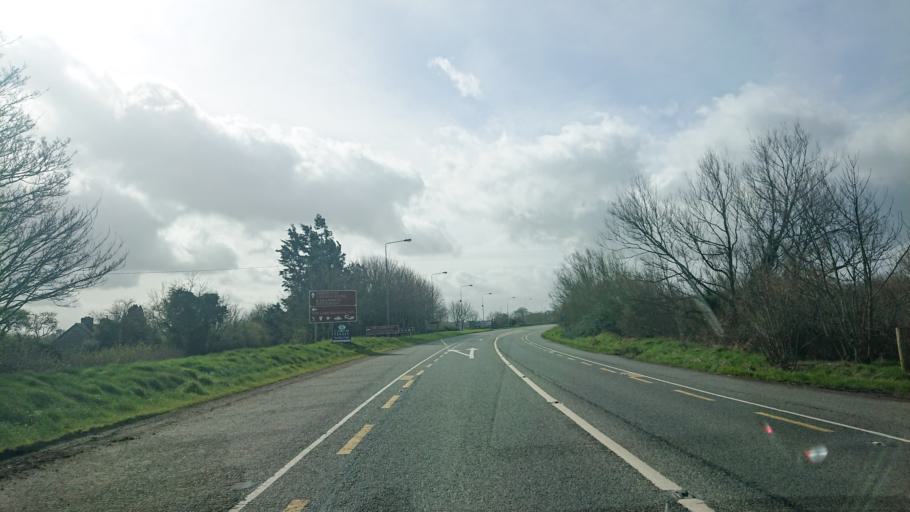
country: IE
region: Leinster
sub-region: County Carlow
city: Bagenalstown
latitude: 52.7463
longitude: -6.9682
